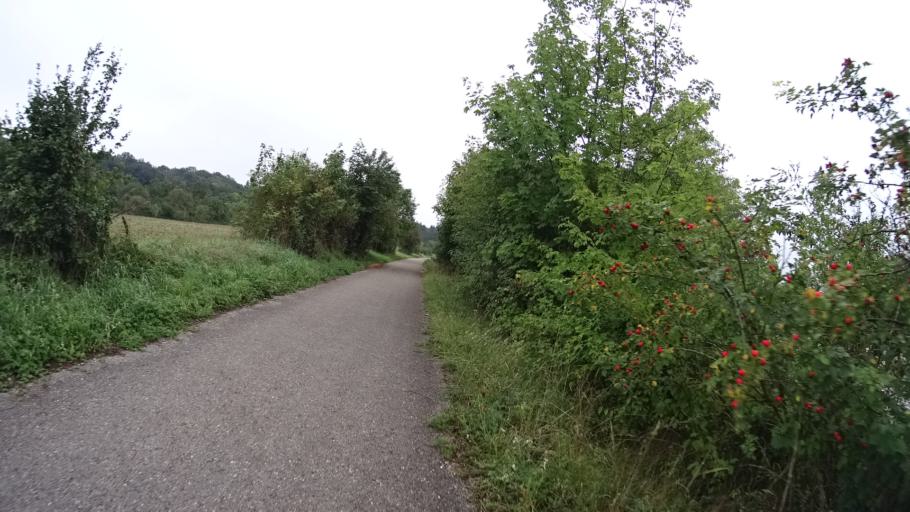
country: DE
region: Bavaria
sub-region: Upper Bavaria
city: Wettstetten
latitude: 48.8212
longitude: 11.4341
